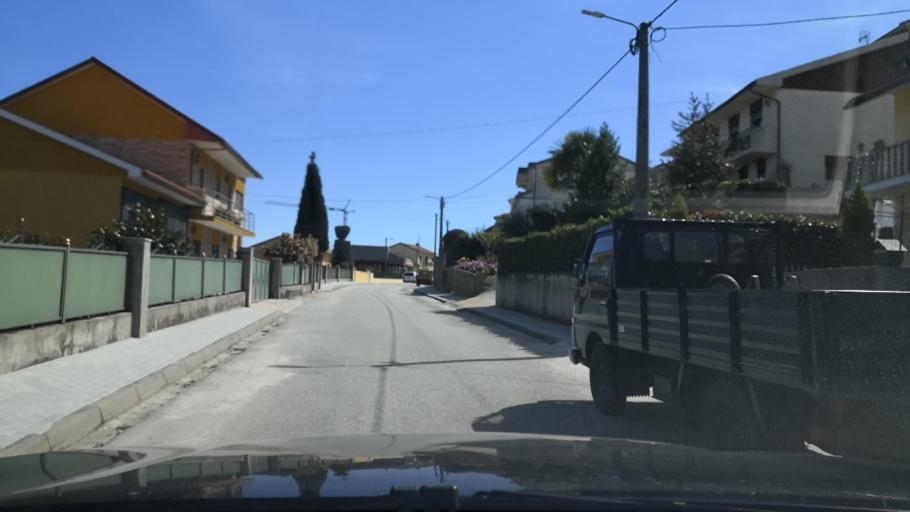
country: PT
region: Vila Real
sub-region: Sabrosa
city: Sabrosa
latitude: 41.3390
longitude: -7.5916
